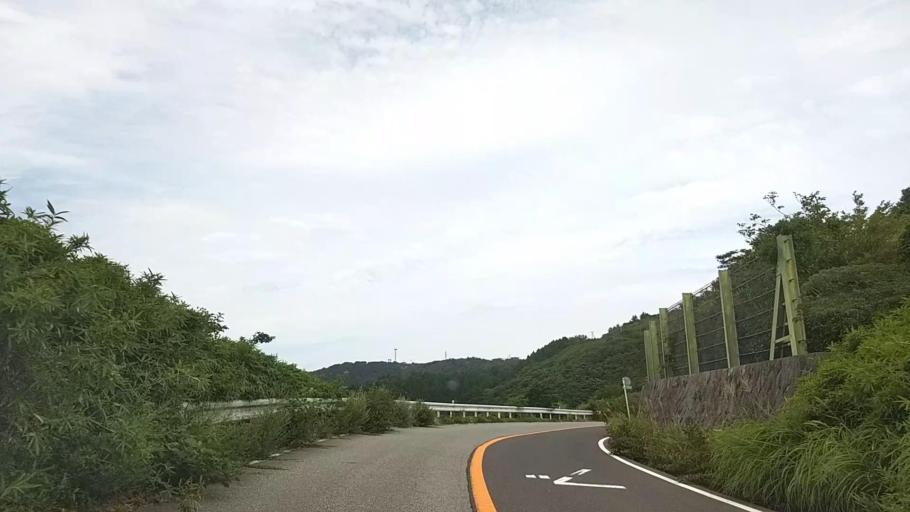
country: JP
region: Kanagawa
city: Hakone
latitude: 35.1806
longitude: 139.0626
